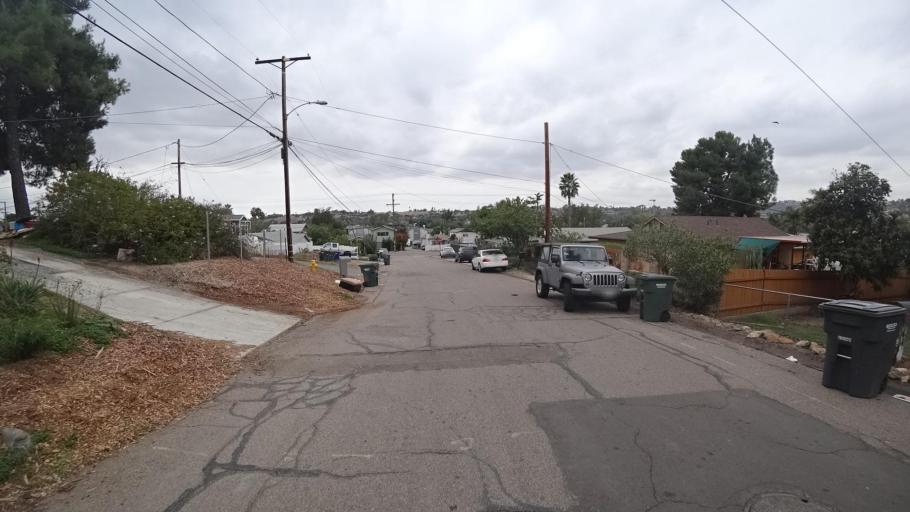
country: US
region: California
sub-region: San Diego County
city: Spring Valley
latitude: 32.7331
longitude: -117.0056
